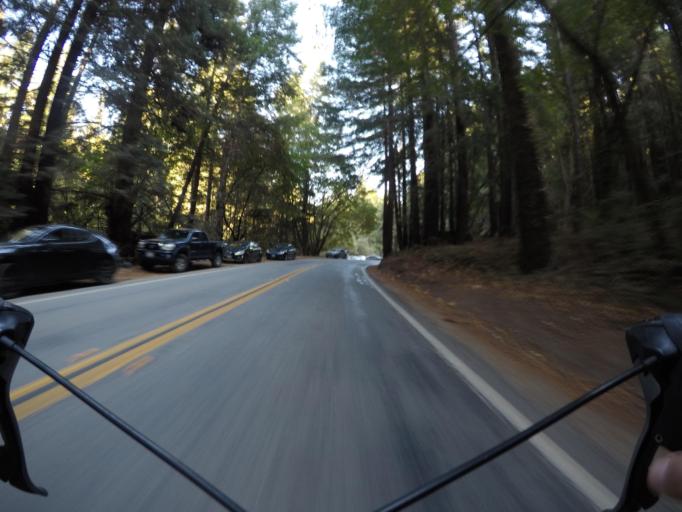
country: US
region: California
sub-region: Santa Cruz County
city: Pasatiempo
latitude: 37.0125
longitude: -122.0559
